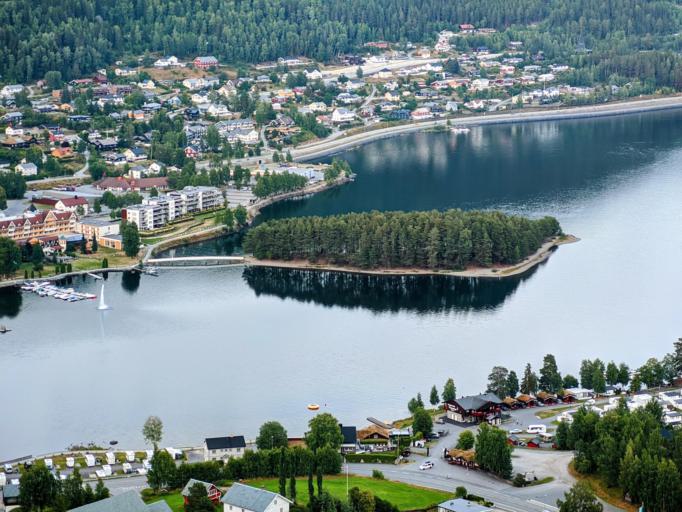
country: NO
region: Oppland
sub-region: Nord-Aurdal
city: Fagernes
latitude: 60.9807
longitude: 9.2211
